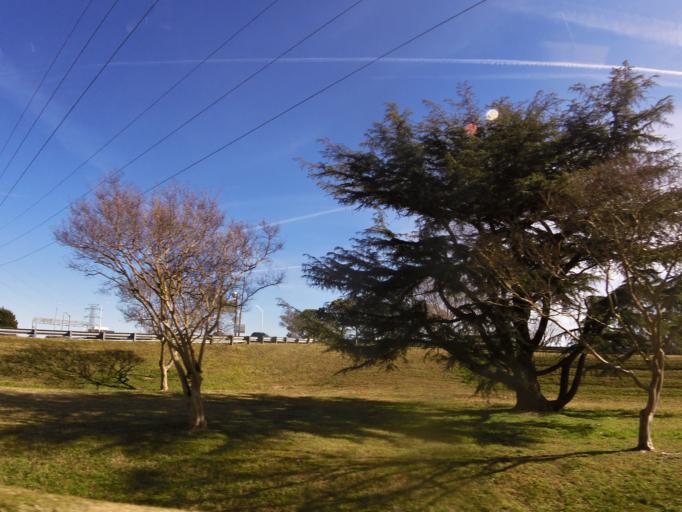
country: US
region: Virginia
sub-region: City of Newport News
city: Newport News
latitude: 37.0174
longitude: -76.4516
